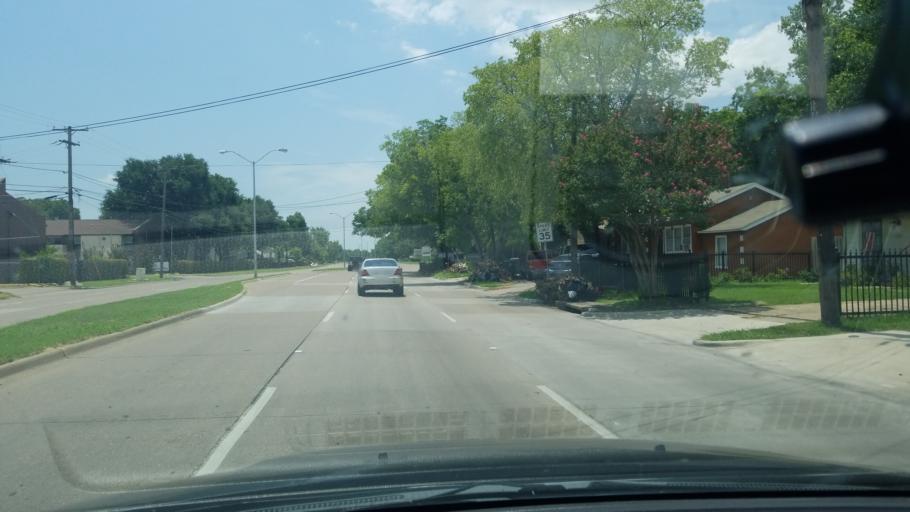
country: US
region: Texas
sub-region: Dallas County
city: Balch Springs
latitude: 32.7336
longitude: -96.6657
